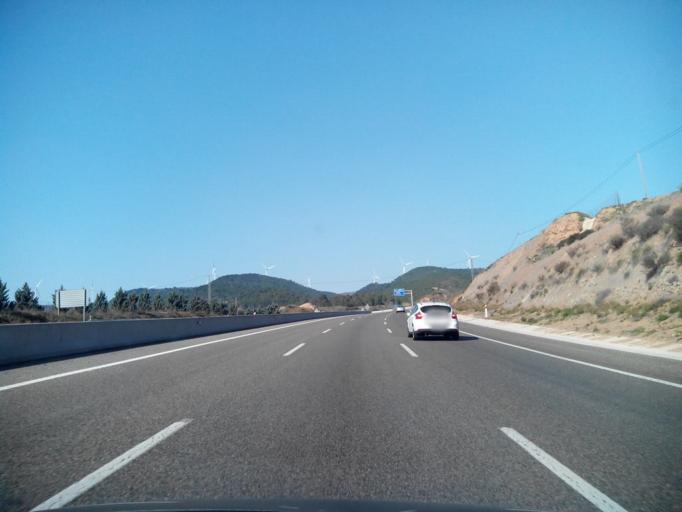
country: ES
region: Catalonia
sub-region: Provincia de Lleida
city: Sant Guim de Freixenet
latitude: 41.6295
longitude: 1.4774
